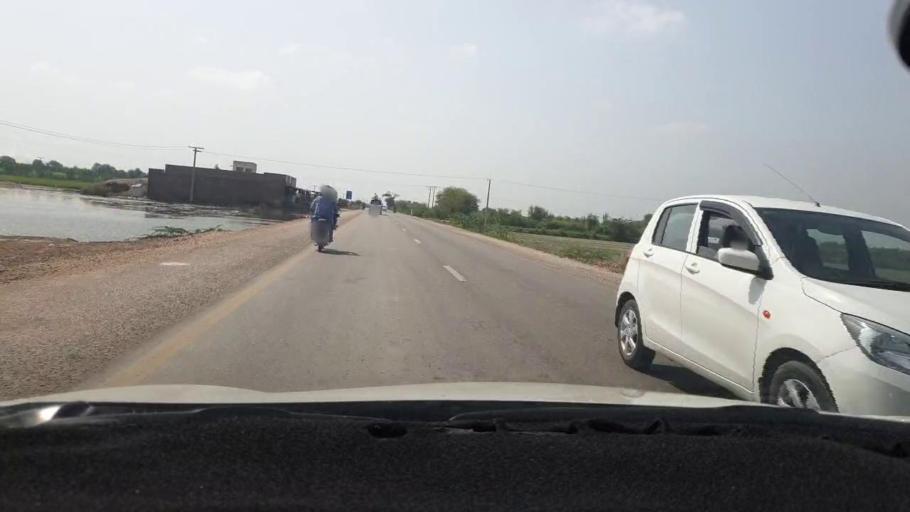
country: PK
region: Sindh
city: Mirpur Khas
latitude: 25.6067
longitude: 69.0832
